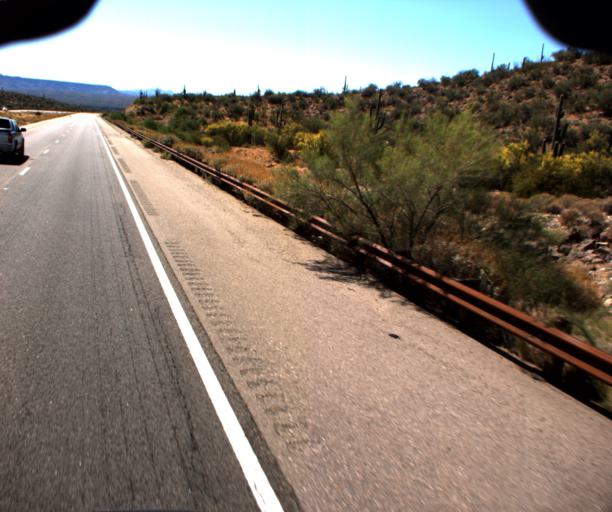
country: US
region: Arizona
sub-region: Yavapai County
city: Bagdad
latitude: 34.3975
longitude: -113.2151
